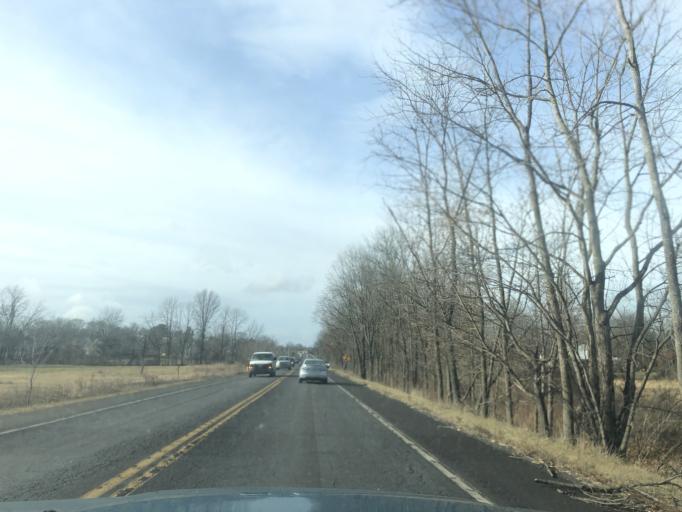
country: US
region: Pennsylvania
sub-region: Bucks County
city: Spinnerstown
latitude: 40.4396
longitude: -75.3959
